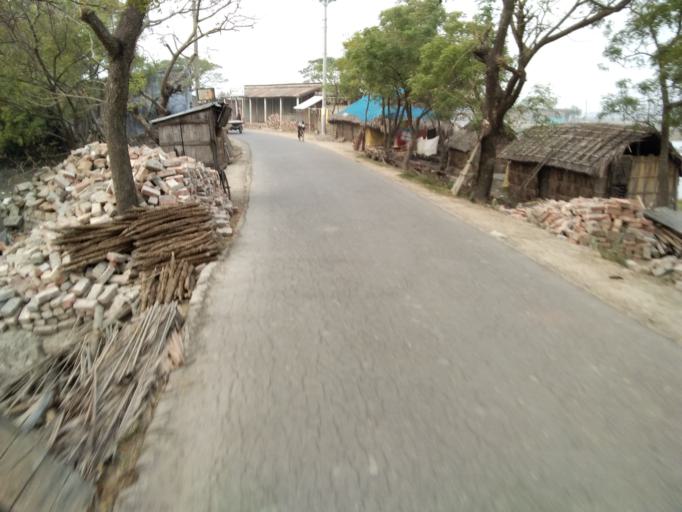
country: BD
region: Khulna
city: Satkhira
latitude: 22.5865
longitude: 89.0656
